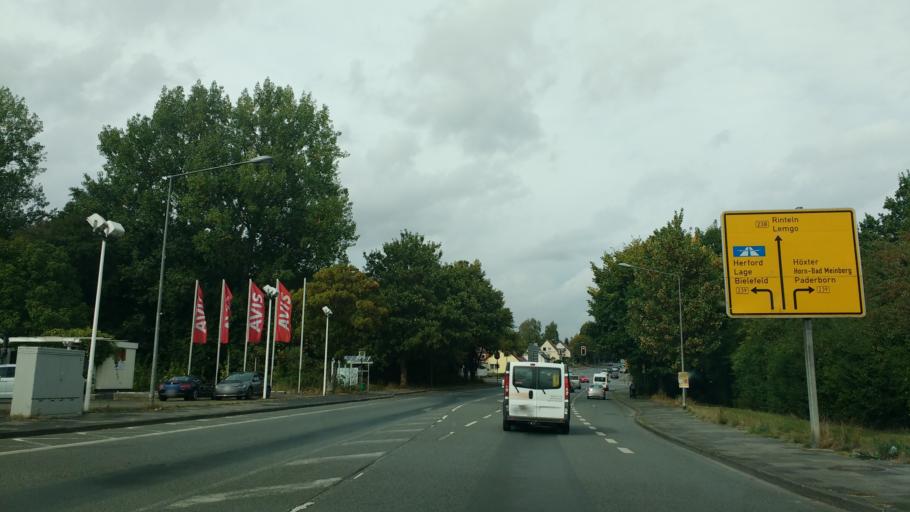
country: DE
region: North Rhine-Westphalia
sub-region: Regierungsbezirk Detmold
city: Detmold
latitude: 51.9529
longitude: 8.8797
